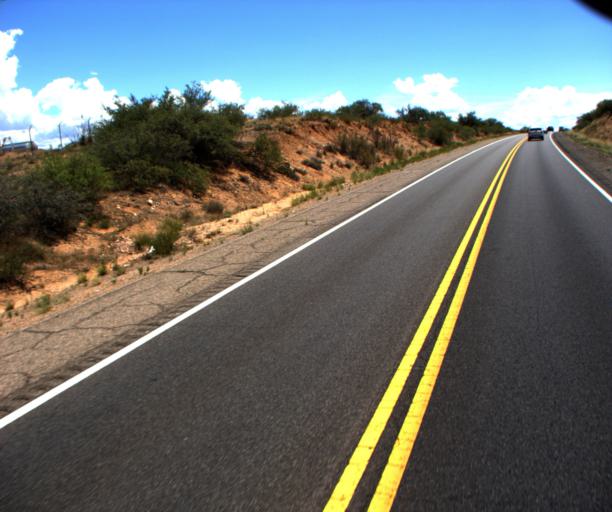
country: US
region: Arizona
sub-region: Yavapai County
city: Camp Verde
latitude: 34.6164
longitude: -111.9170
